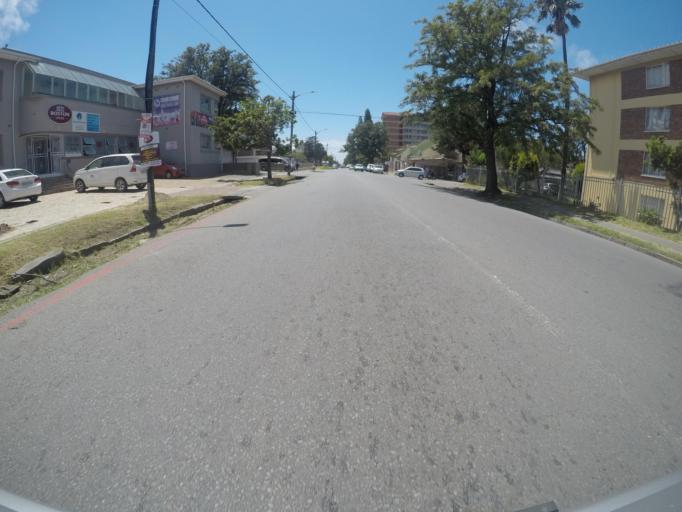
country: ZA
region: Eastern Cape
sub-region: Buffalo City Metropolitan Municipality
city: East London
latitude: -33.0033
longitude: 27.9007
